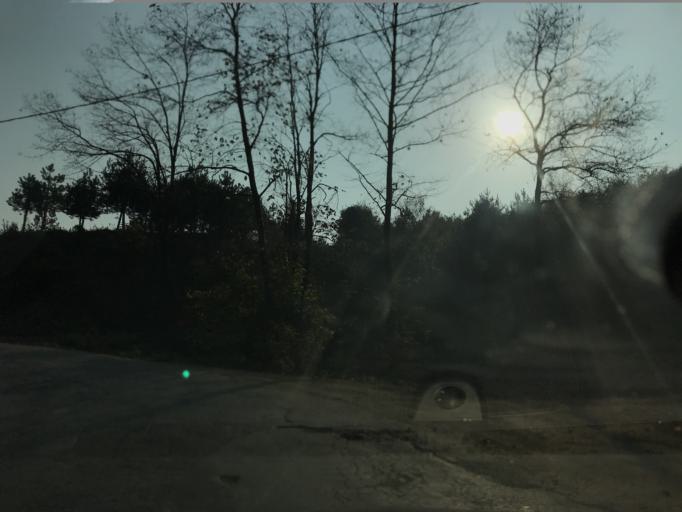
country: TR
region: Duzce
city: Cumayeri
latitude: 40.9129
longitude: 30.9398
